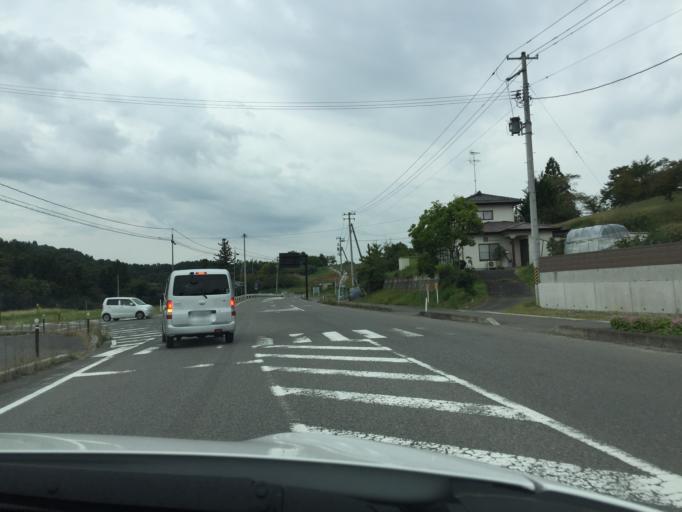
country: JP
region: Fukushima
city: Fukushima-shi
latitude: 37.6530
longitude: 140.5316
